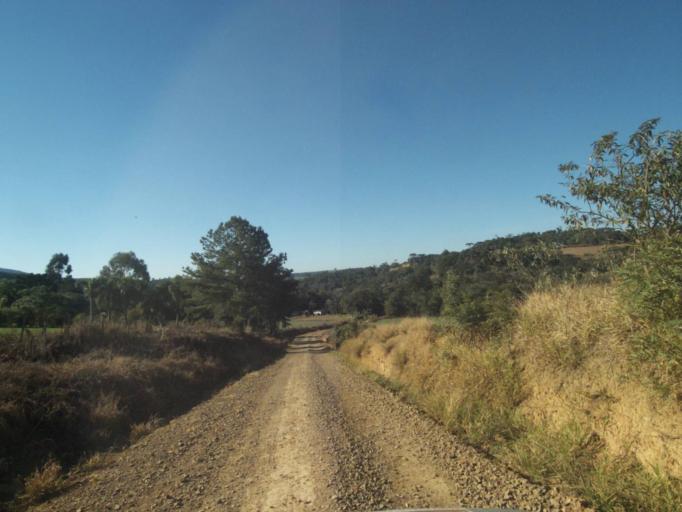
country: BR
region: Parana
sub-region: Tibagi
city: Tibagi
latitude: -24.5527
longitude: -50.5208
